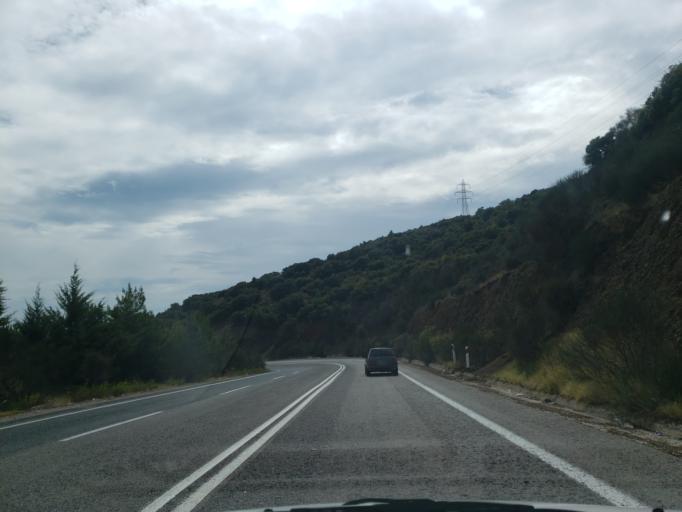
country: GR
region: Central Greece
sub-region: Nomos Fthiotidos
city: Stavros
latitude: 38.9787
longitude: 22.3796
